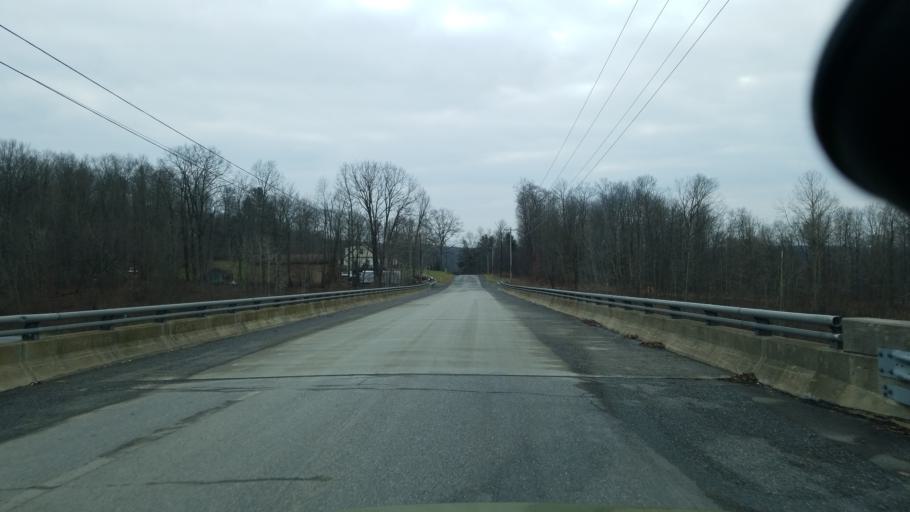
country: US
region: Pennsylvania
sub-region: Clearfield County
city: Treasure Lake
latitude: 41.1248
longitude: -78.6883
